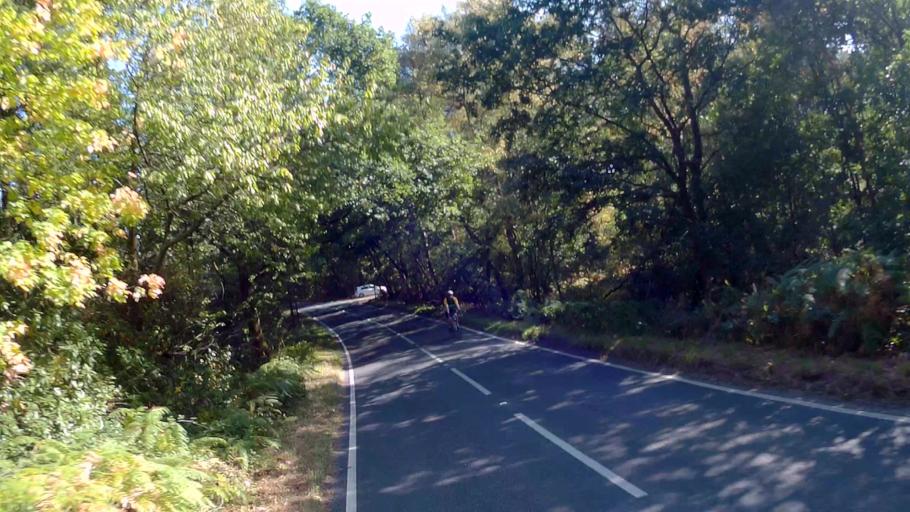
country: GB
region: England
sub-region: Surrey
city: Farnham
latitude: 51.1915
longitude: -0.7687
